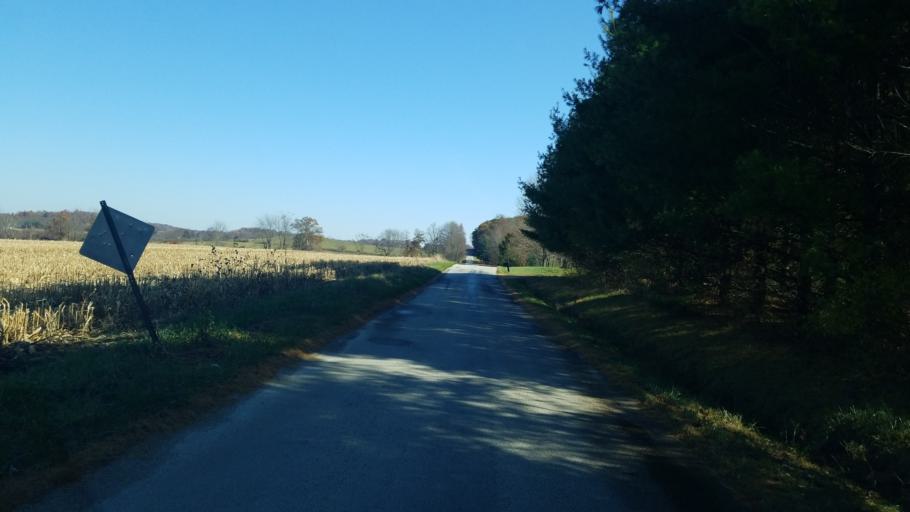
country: US
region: Ohio
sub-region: Licking County
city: Newark
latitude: 40.1024
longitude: -82.3723
